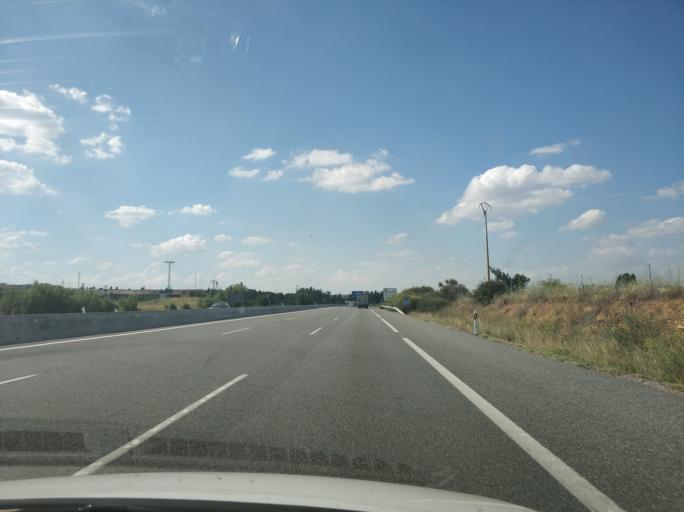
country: ES
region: Castille and Leon
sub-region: Provincia de Zamora
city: Benavente
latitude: 42.0092
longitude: -5.6623
